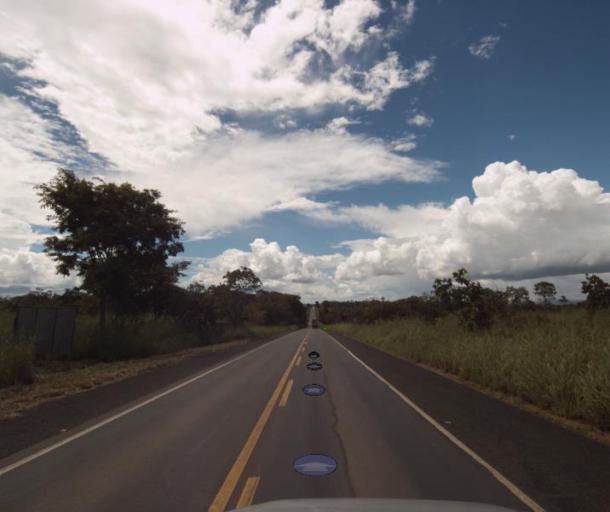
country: BR
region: Goias
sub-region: Uruacu
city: Uruacu
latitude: -14.1533
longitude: -49.1200
